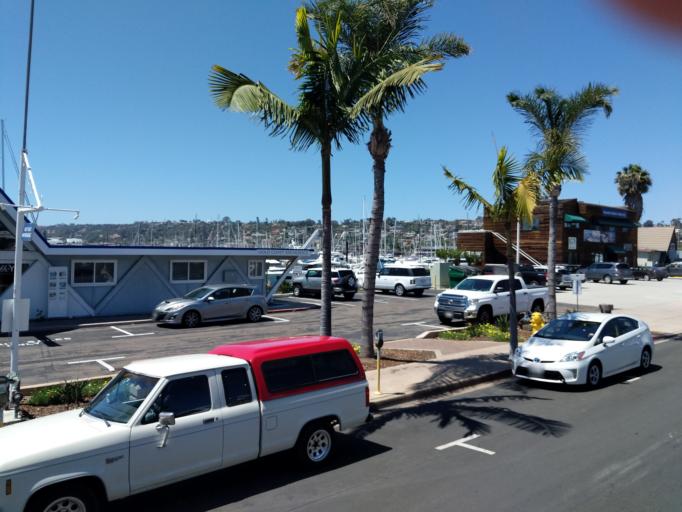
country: US
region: California
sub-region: San Diego County
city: Coronado
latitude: 32.7190
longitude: -117.2248
